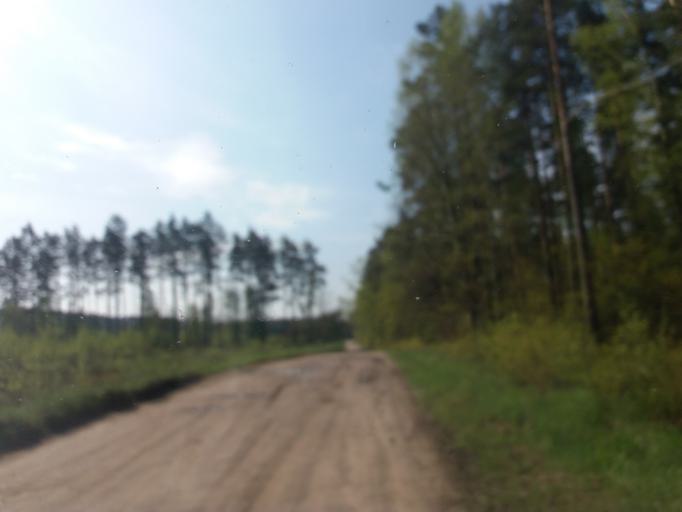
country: PL
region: West Pomeranian Voivodeship
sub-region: Powiat choszczenski
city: Drawno
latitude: 53.2370
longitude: 15.8194
